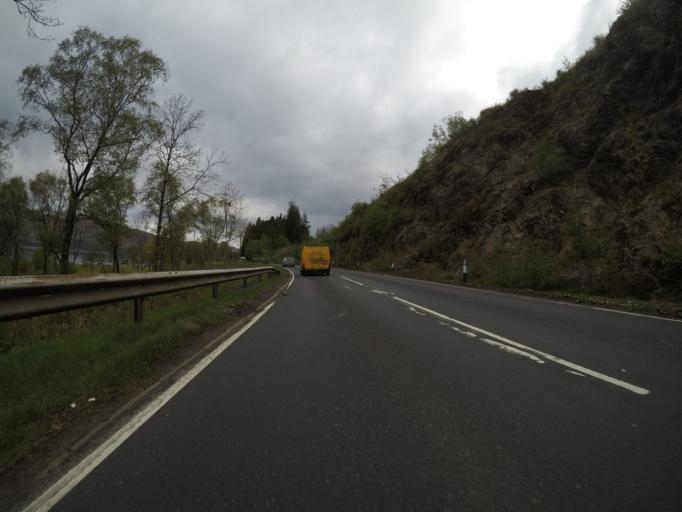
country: GB
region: Scotland
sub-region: Highland
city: Fort William
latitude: 56.7404
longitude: -5.2071
